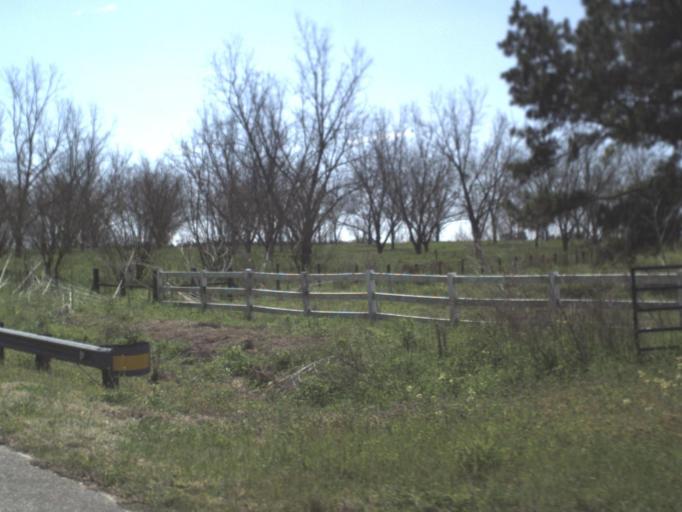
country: US
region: Florida
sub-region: Jefferson County
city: Monticello
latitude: 30.3729
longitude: -83.9972
